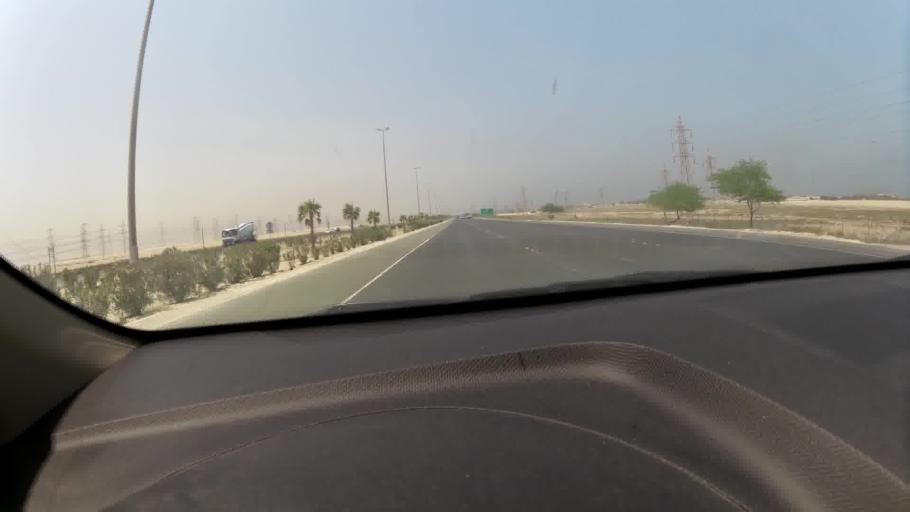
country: KW
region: Al Ahmadi
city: Al Fahahil
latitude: 28.8928
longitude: 48.2230
